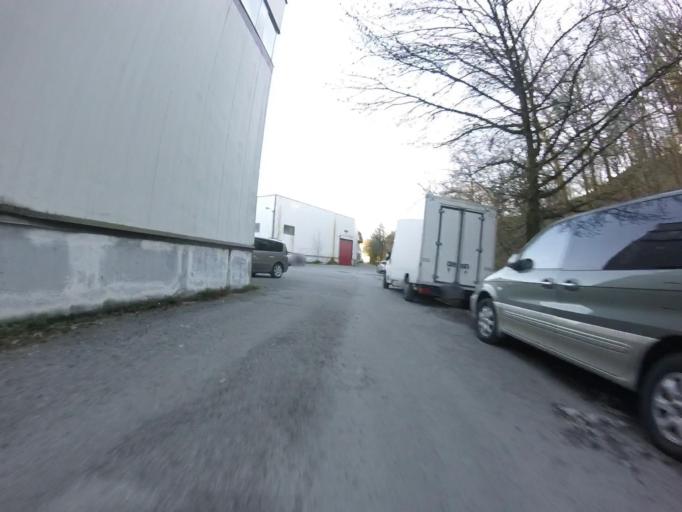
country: ES
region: Basque Country
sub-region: Provincia de Guipuzcoa
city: Errenteria
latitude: 43.2991
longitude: -1.8846
